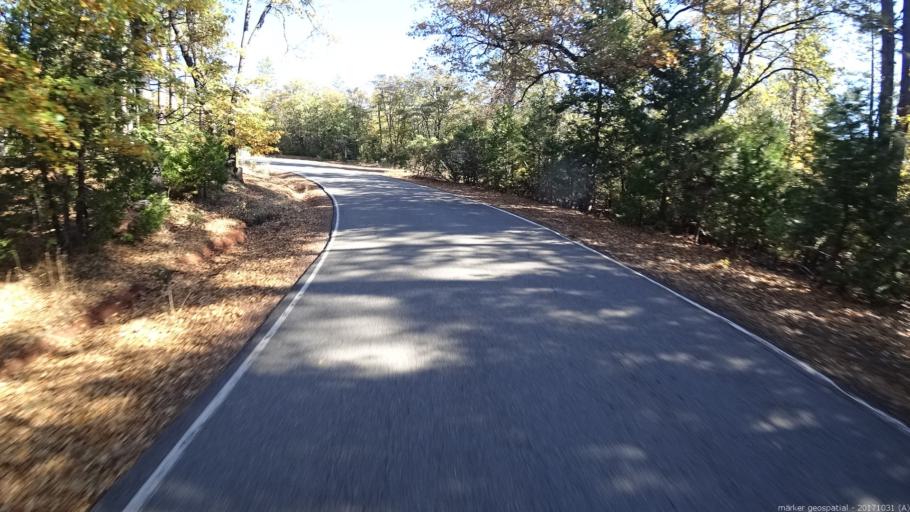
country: US
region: California
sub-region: Shasta County
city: Shingletown
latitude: 40.4734
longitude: -121.8754
